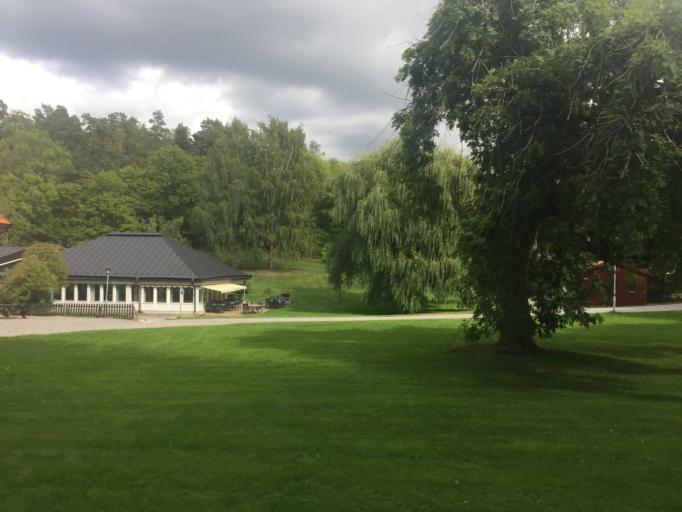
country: SE
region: Stockholm
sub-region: Salems Kommun
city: Ronninge
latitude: 59.2615
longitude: 17.7120
